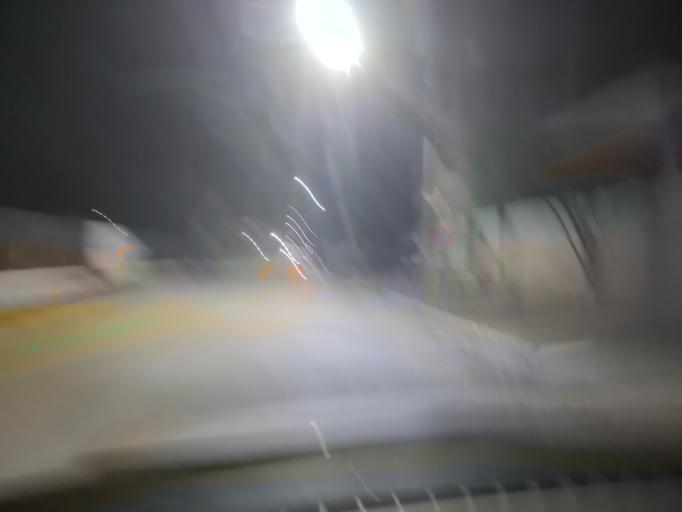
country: BR
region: Minas Gerais
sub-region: Governador Valadares
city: Governador Valadares
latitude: -18.8768
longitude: -41.9669
